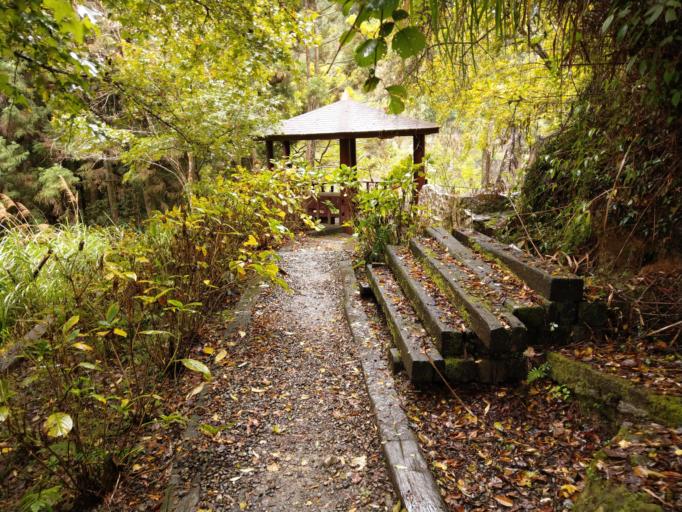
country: TW
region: Taiwan
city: Lugu
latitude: 23.6385
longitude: 120.7834
